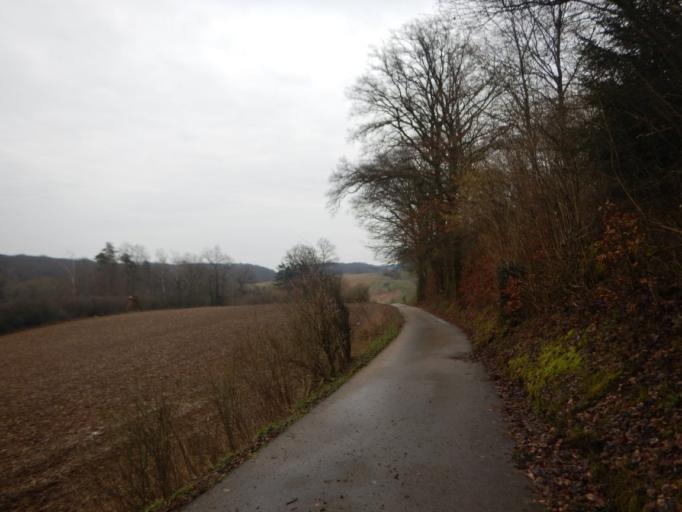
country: LU
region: Luxembourg
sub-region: Canton de Capellen
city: Koerich
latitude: 49.6758
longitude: 5.9545
